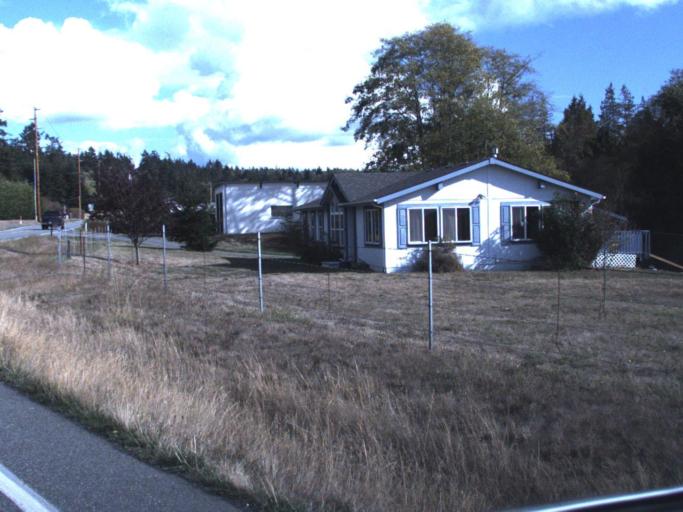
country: US
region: Washington
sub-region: Island County
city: Coupeville
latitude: 48.1709
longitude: -122.6367
